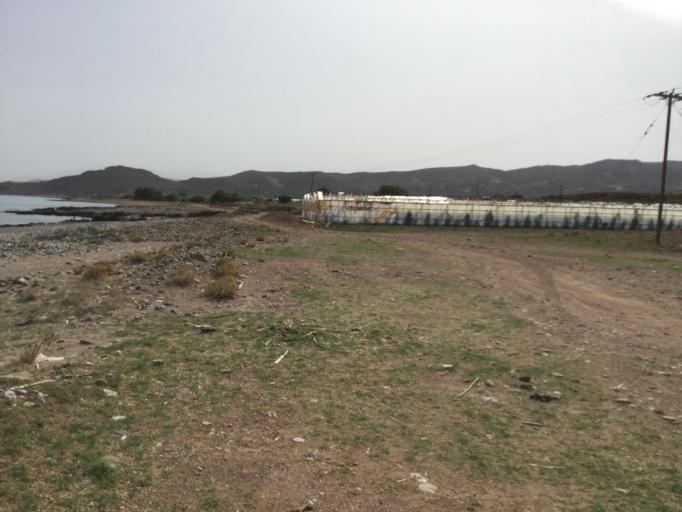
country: GR
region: Crete
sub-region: Nomos Chanias
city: Kissamos
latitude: 35.5199
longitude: 23.6117
